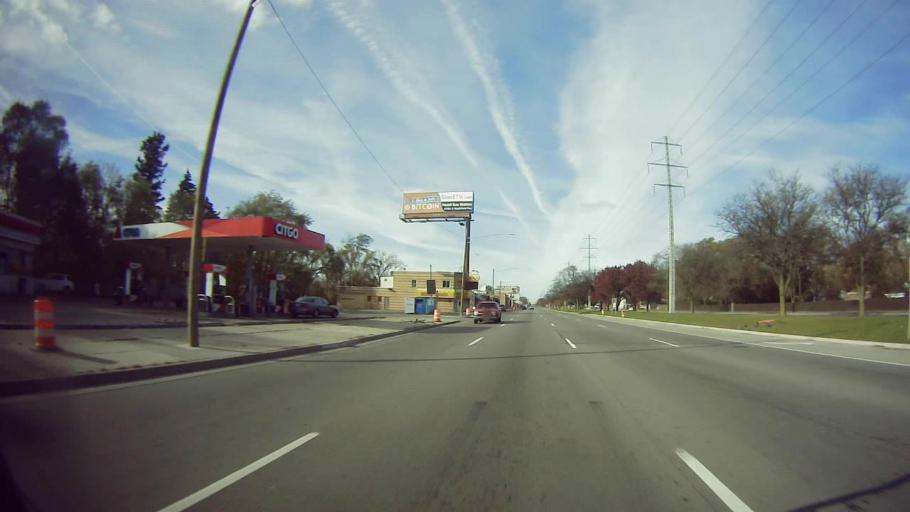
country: US
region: Michigan
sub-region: Oakland County
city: Southfield
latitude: 42.4441
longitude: -83.2228
